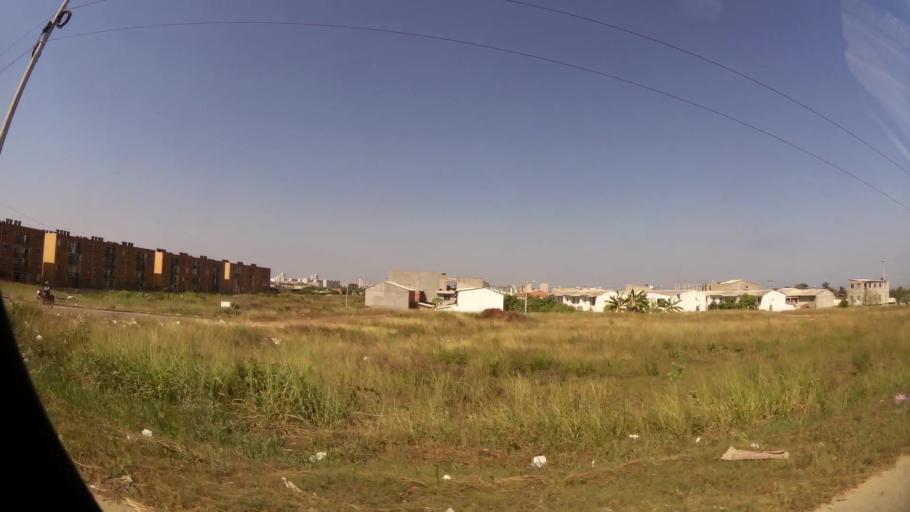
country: CO
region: Bolivar
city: Cartagena
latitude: 10.3915
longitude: -75.4483
